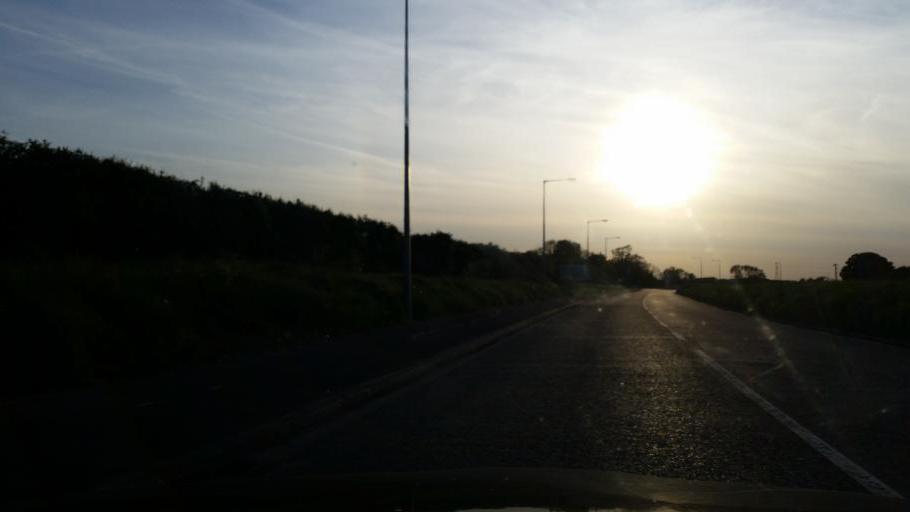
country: IE
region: Leinster
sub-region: Fingal County
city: Swords
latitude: 53.4893
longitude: -6.1924
